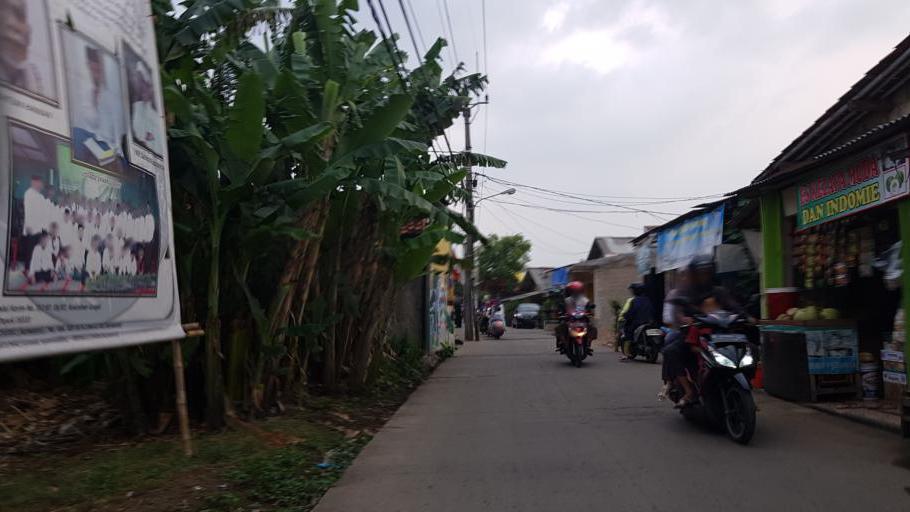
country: ID
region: West Java
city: Sawangan
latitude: -6.3799
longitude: 106.7935
